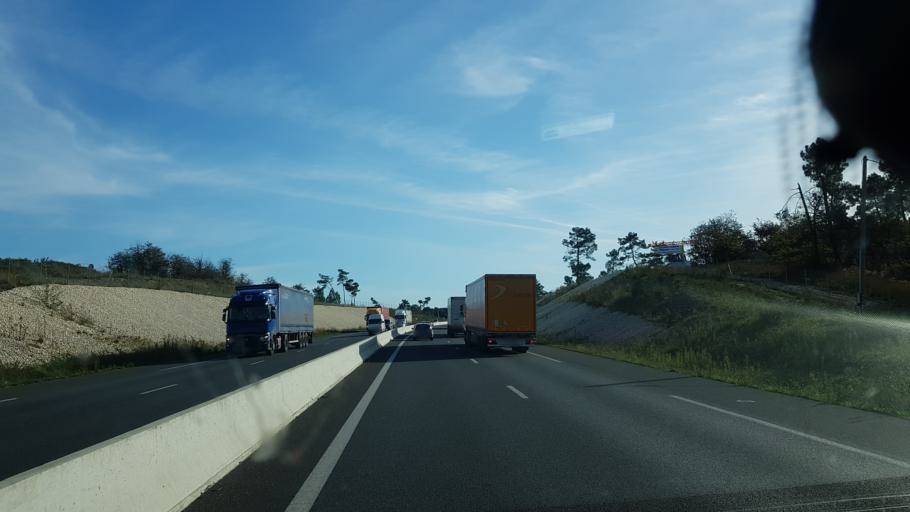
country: FR
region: Poitou-Charentes
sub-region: Departement de la Charente
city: Baignes-Sainte-Radegonde
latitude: 45.3764
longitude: -0.1814
